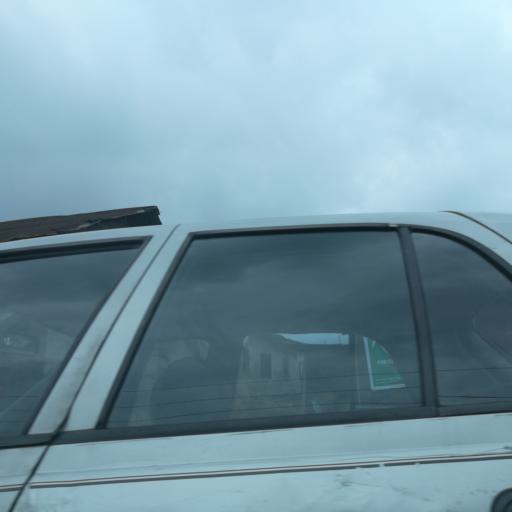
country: NG
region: Rivers
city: Port Harcourt
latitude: 4.8111
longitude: 7.0499
